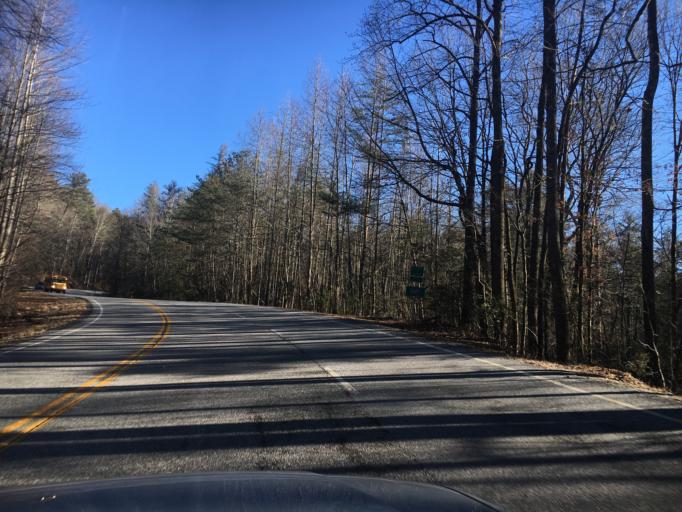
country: US
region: Georgia
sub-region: Lumpkin County
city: Dahlonega
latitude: 34.6914
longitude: -83.9113
